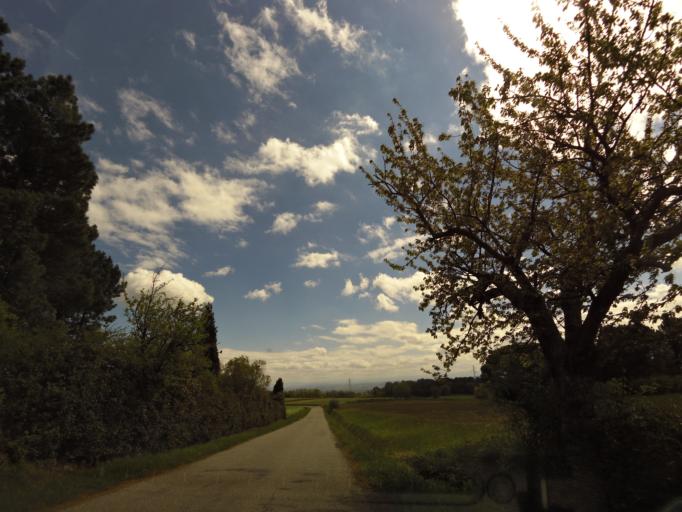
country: FR
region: Languedoc-Roussillon
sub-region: Departement de l'Aude
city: Saint-Martin-Lalande
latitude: 43.3563
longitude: 2.0561
